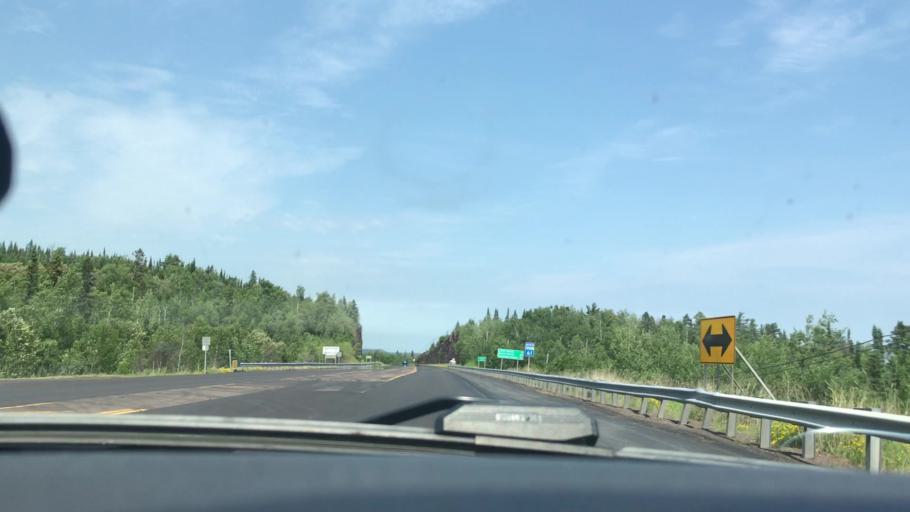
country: US
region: Minnesota
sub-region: Lake County
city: Silver Bay
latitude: 47.3467
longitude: -91.1874
